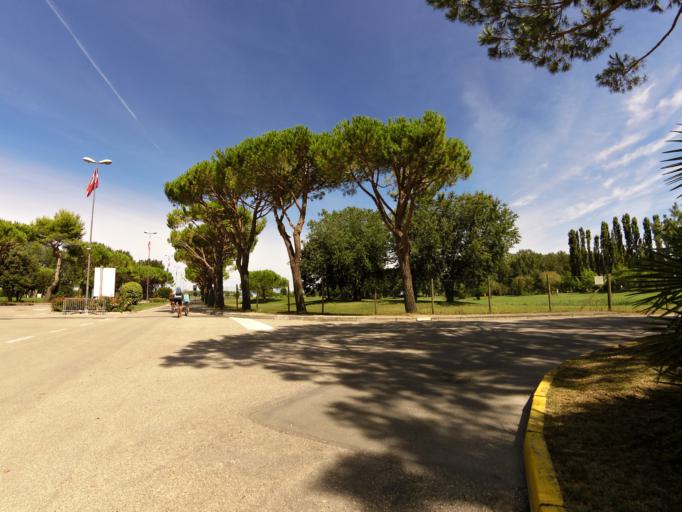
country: IT
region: Veneto
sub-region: Provincia di Venezia
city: Caorle
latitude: 45.5742
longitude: 12.8113
